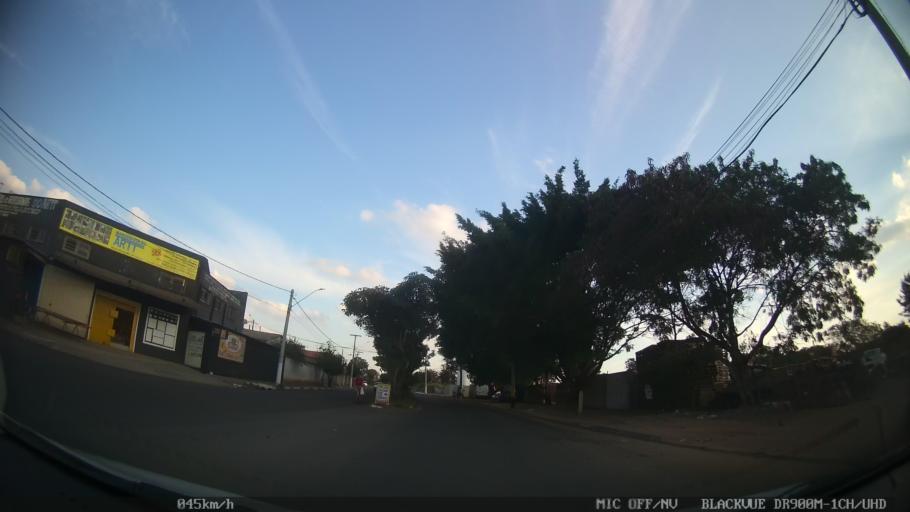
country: BR
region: Sao Paulo
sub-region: Hortolandia
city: Hortolandia
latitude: -22.8606
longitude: -47.1791
